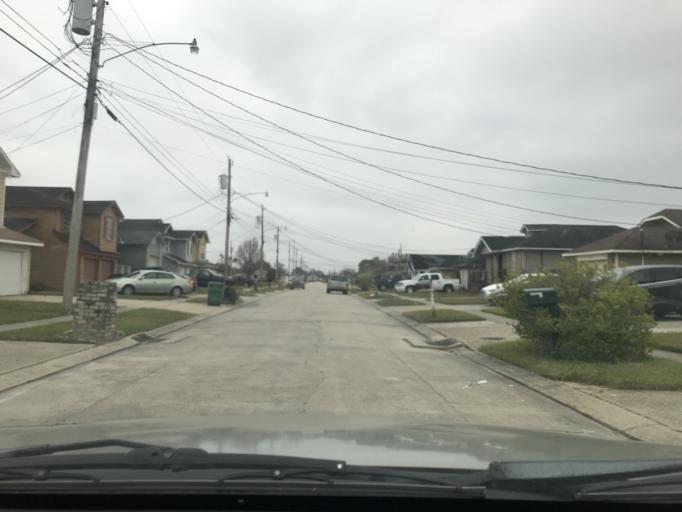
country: US
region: Louisiana
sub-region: Jefferson Parish
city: Woodmere
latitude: 29.8654
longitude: -90.0752
